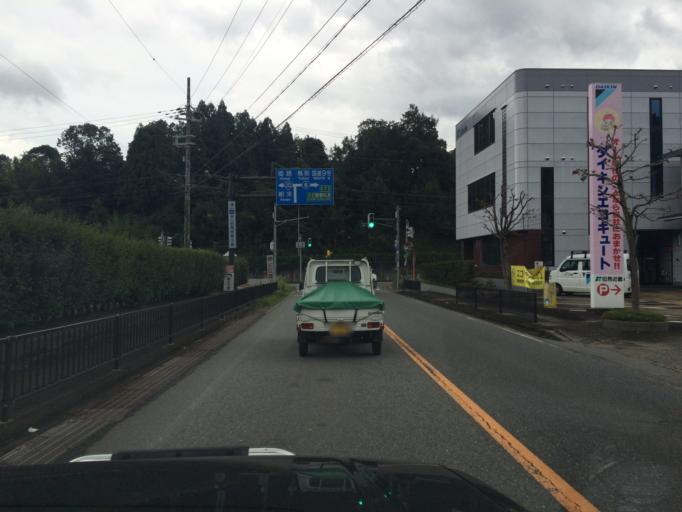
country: JP
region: Hyogo
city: Toyooka
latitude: 35.4042
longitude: 134.7773
